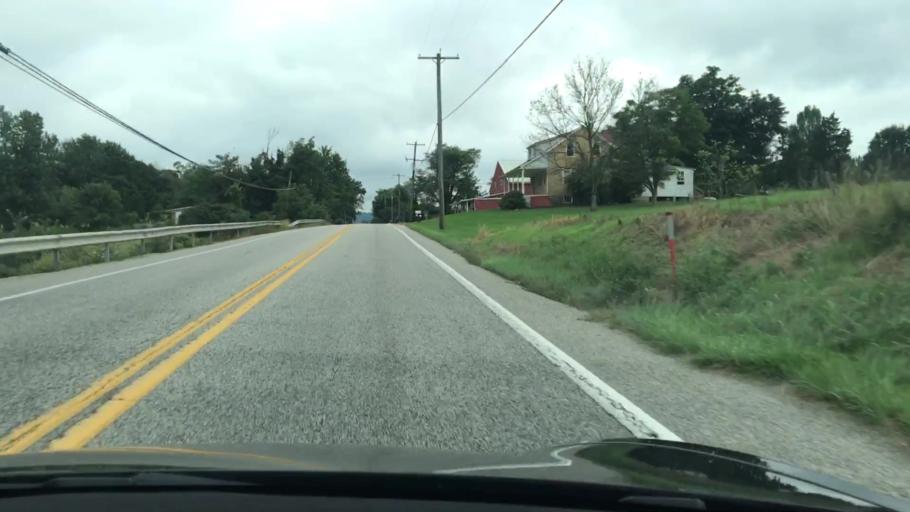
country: US
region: Pennsylvania
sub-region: Cumberland County
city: Shiremanstown
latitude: 40.1519
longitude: -76.9667
